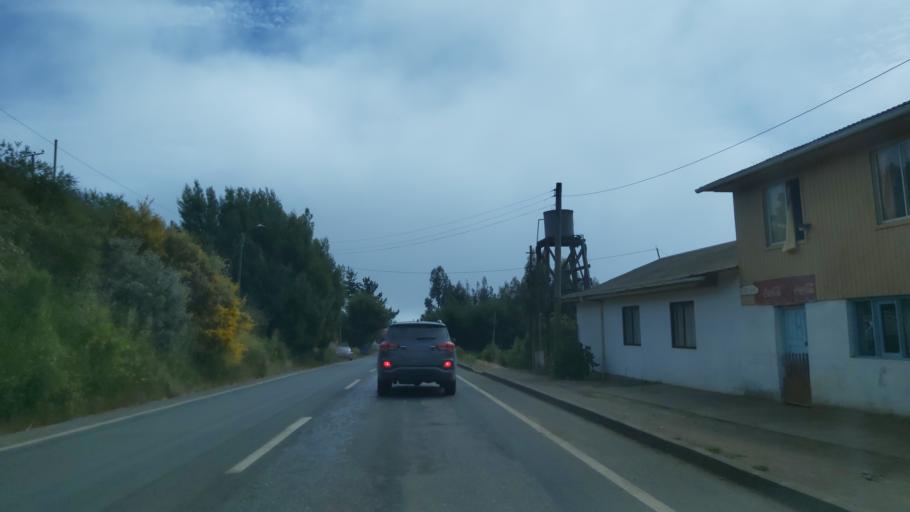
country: CL
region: Maule
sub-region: Provincia de Cauquenes
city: Cauquenes
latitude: -35.8704
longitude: -72.6567
